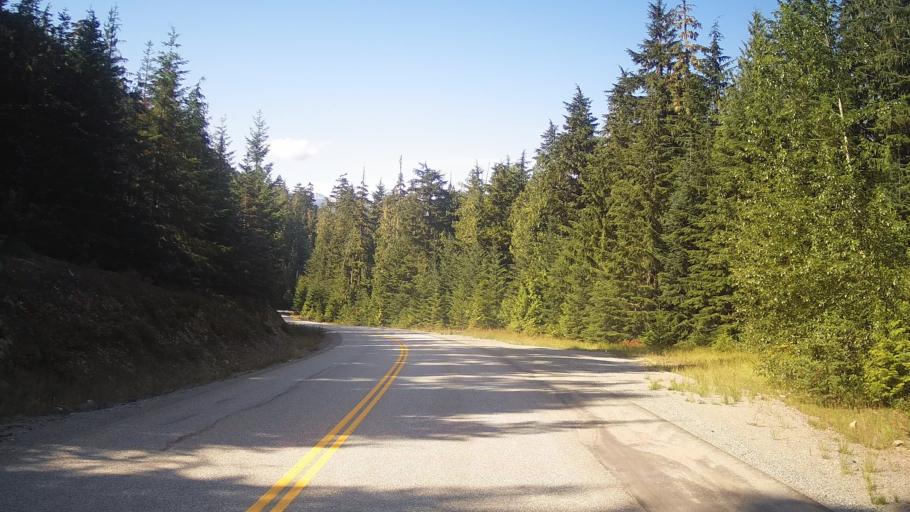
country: CA
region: British Columbia
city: Pemberton
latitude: 50.3446
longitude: -122.5358
